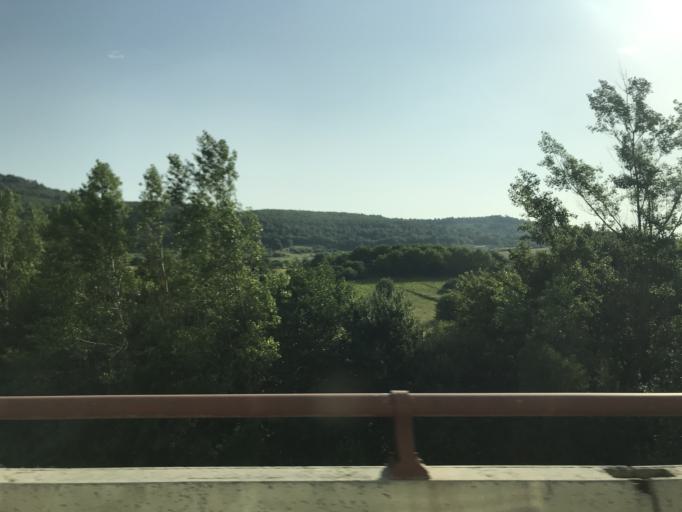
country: ES
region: Navarre
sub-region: Provincia de Navarra
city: Altsasu
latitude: 42.9124
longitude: -2.1795
